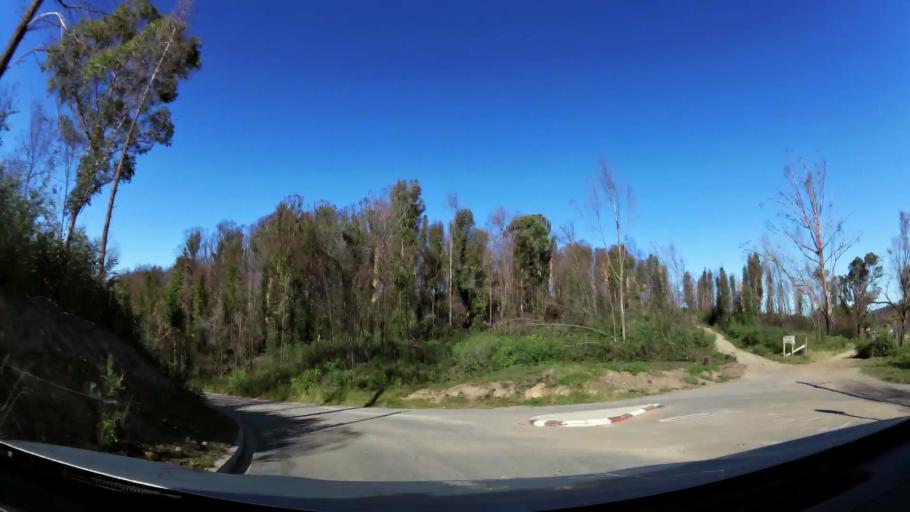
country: ZA
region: Western Cape
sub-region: Eden District Municipality
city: Knysna
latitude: -34.0241
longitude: 23.0076
